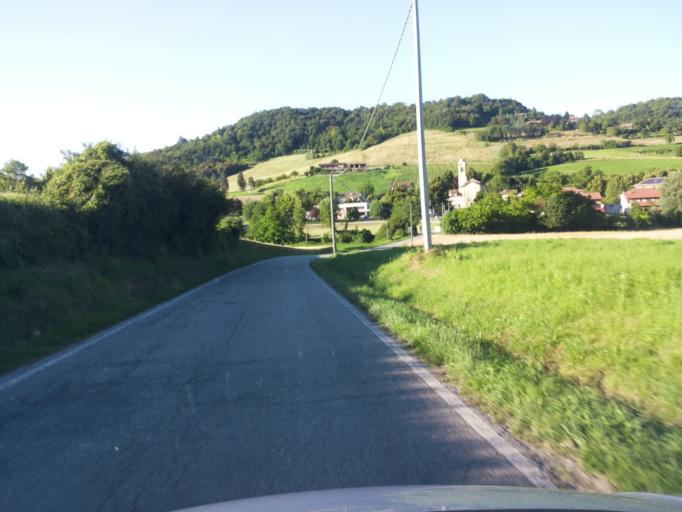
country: IT
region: Piedmont
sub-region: Provincia di Alessandria
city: Murisengo
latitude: 45.0853
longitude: 8.1462
